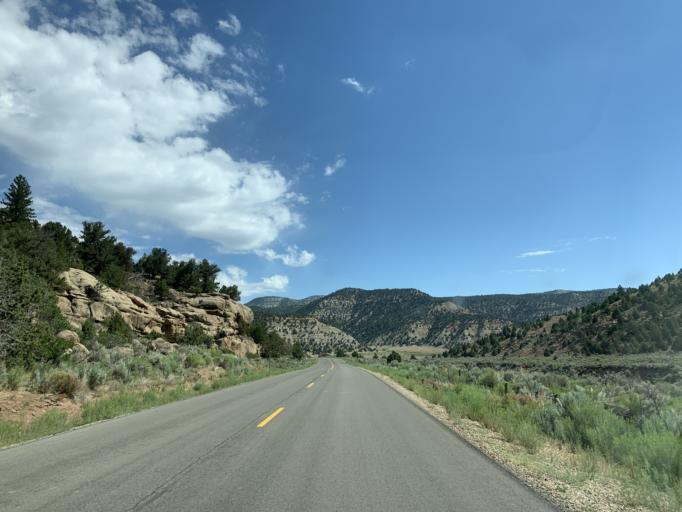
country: US
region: Utah
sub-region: Carbon County
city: East Carbon City
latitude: 39.7671
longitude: -110.5191
